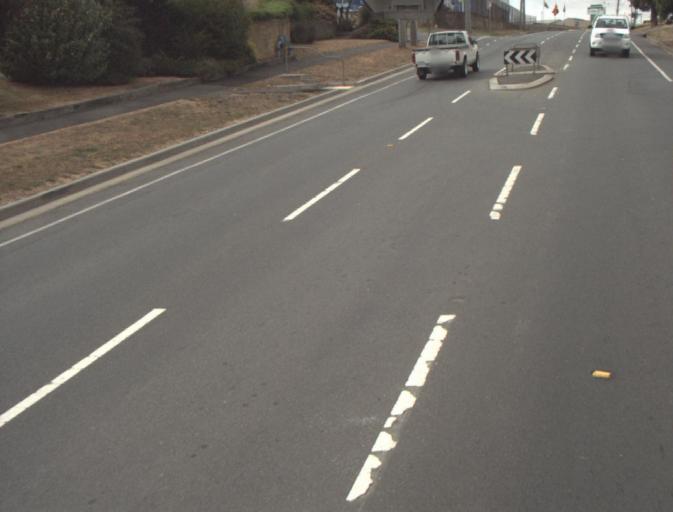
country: AU
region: Tasmania
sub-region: Launceston
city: Summerhill
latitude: -41.4801
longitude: 147.1668
